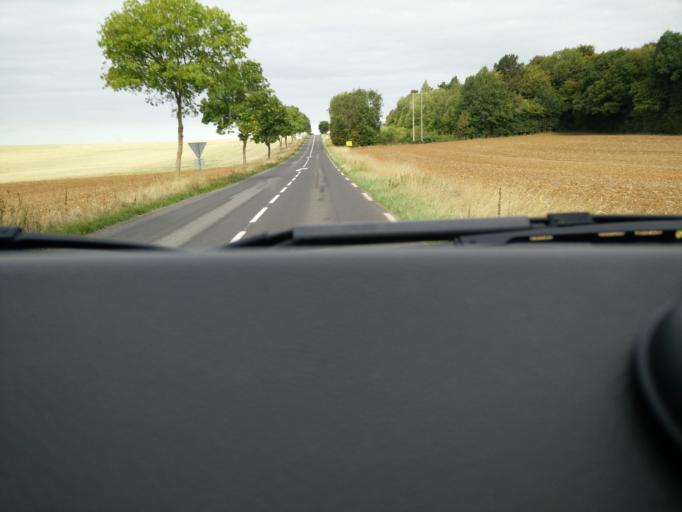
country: FR
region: Lorraine
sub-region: Departement de Meurthe-et-Moselle
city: Montauville
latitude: 48.8954
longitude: 5.9749
